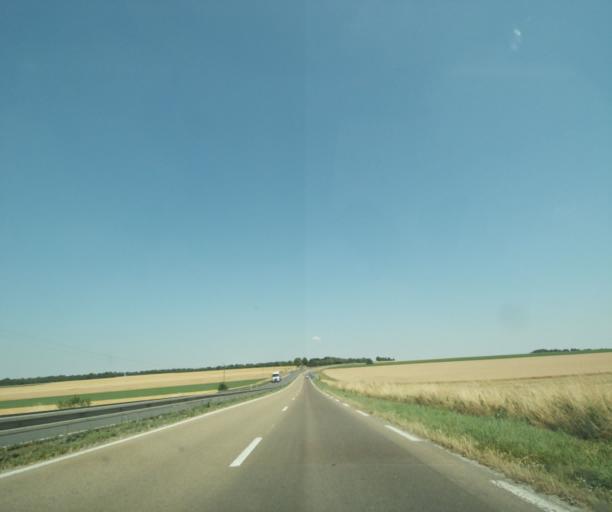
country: FR
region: Champagne-Ardenne
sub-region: Departement de la Marne
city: Fagnieres
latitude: 49.0086
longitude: 4.3318
